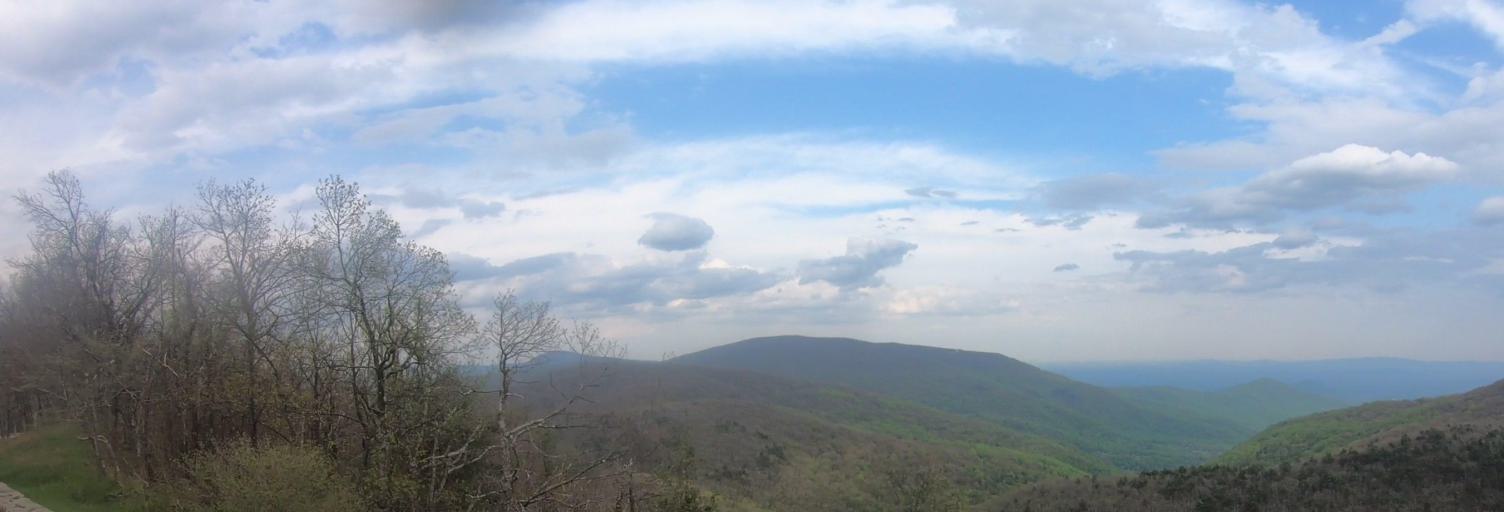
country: US
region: Virginia
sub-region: Rockingham County
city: Elkton
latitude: 38.2832
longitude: -78.6595
